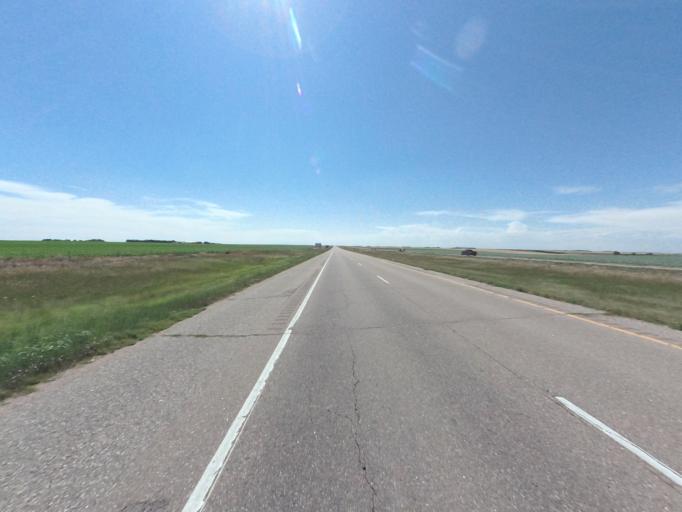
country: US
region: Colorado
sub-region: Kit Carson County
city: Burlington
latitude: 39.2940
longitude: -102.3093
